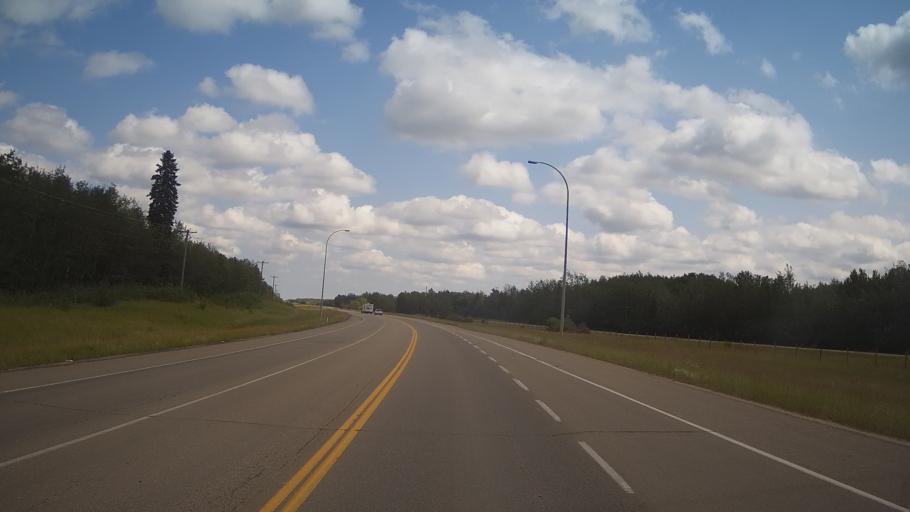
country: CA
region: Alberta
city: Sherwood Park
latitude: 53.3959
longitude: -113.0973
